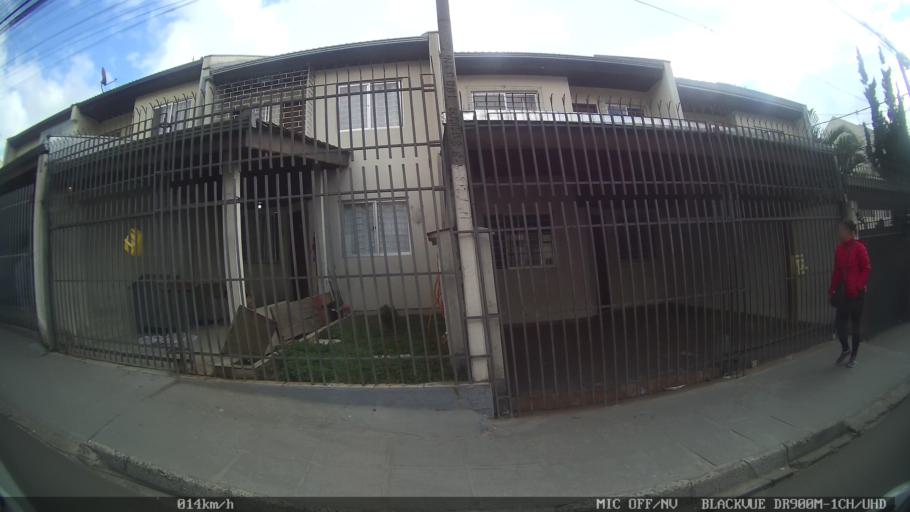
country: BR
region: Parana
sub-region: Pinhais
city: Pinhais
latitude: -25.3739
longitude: -49.2190
